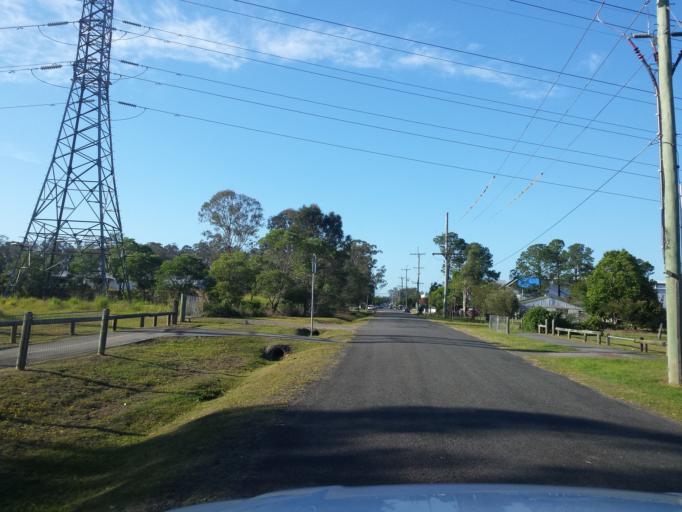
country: AU
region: Queensland
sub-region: Logan
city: Slacks Creek
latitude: -27.6575
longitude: 153.1342
